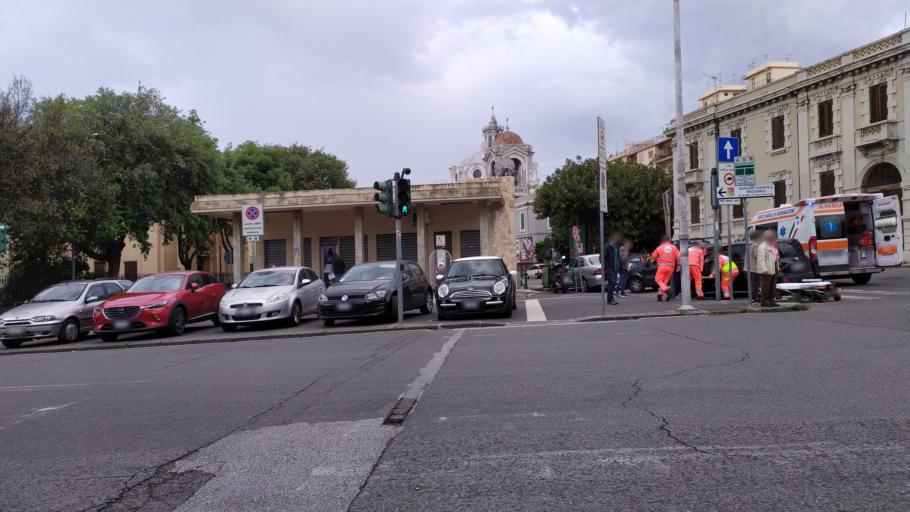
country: IT
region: Sicily
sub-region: Messina
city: Messina
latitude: 38.1894
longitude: 15.5517
